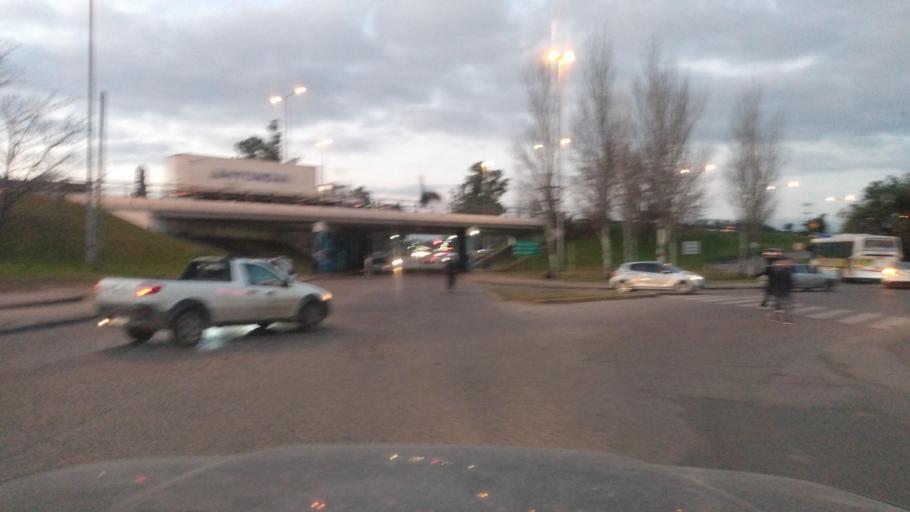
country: AR
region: Buenos Aires
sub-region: Partido de Pilar
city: Pilar
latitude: -34.4502
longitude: -58.9062
